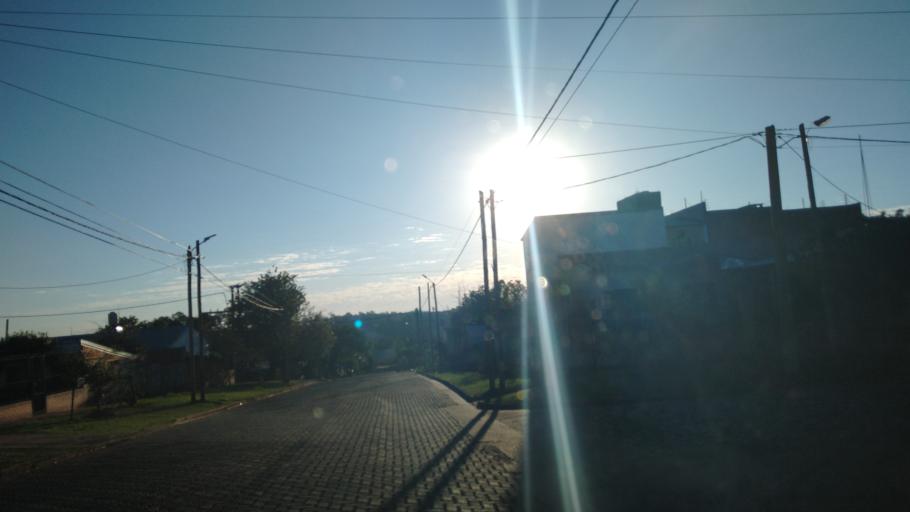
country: AR
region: Misiones
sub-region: Departamento de Capital
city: Posadas
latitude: -27.4133
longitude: -55.9522
